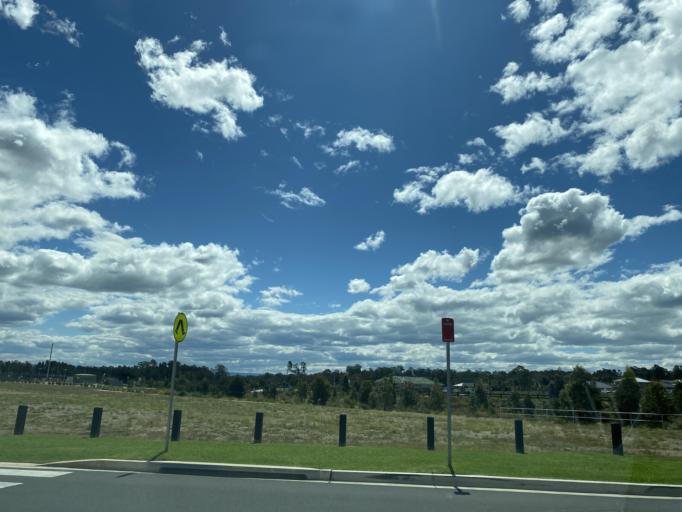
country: AU
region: New South Wales
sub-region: Campbelltown Municipality
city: Denham Court
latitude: -33.9951
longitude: 150.7909
